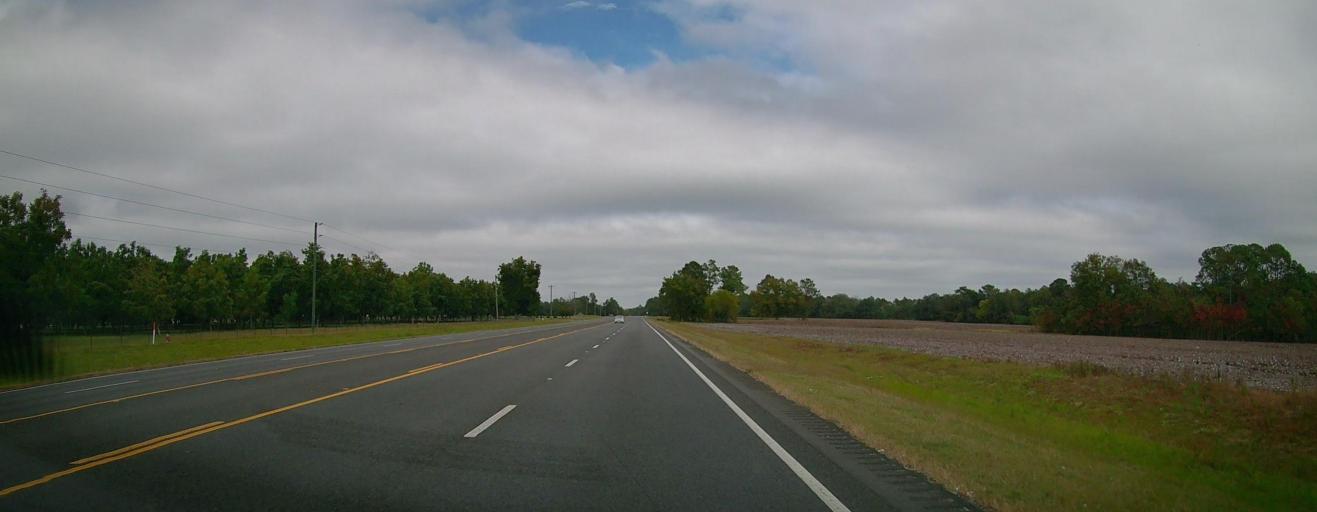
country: US
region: Georgia
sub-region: Thomas County
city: Thomasville
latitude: 30.9920
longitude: -83.8753
